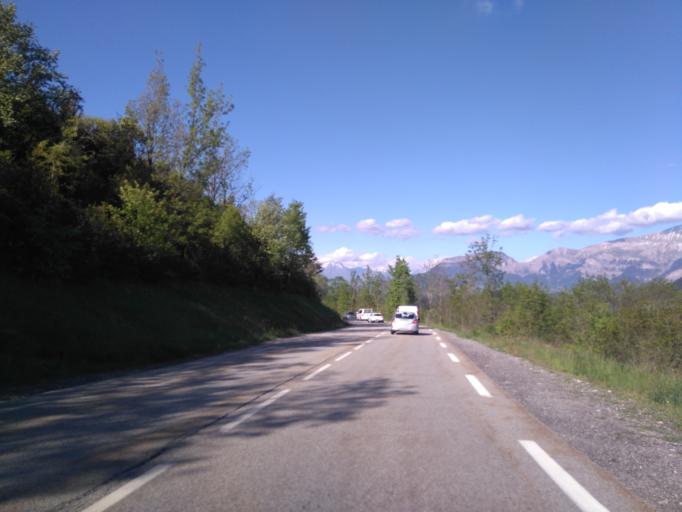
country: FR
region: Rhone-Alpes
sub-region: Departement de l'Isere
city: Mens
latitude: 44.7580
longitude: 5.6656
